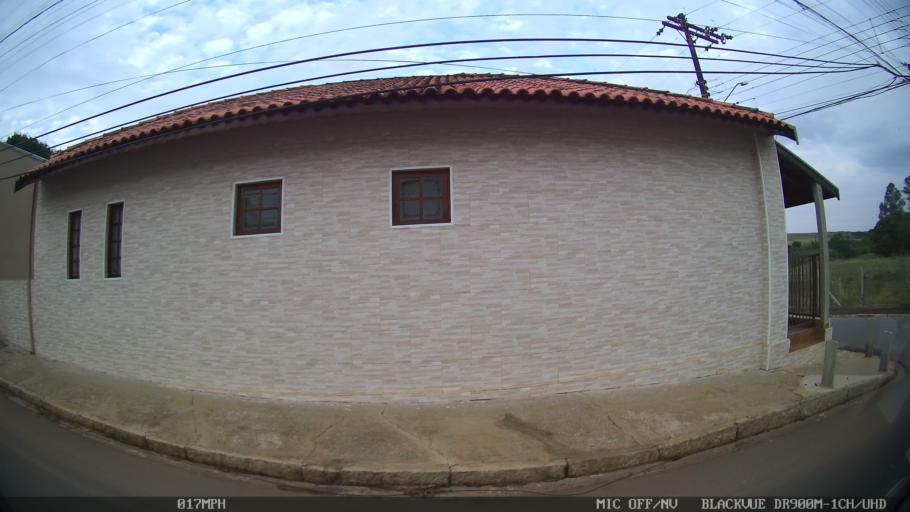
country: BR
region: Sao Paulo
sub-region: Americana
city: Americana
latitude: -22.6523
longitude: -47.3531
